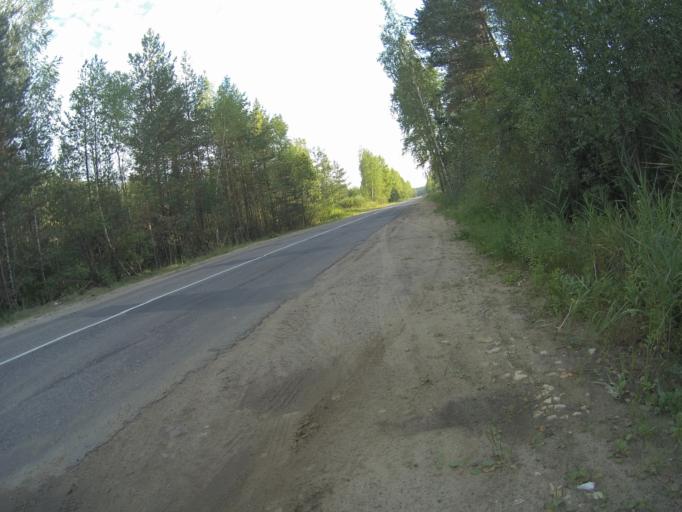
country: RU
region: Vladimir
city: Raduzhnyy
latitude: 55.9809
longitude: 40.3076
